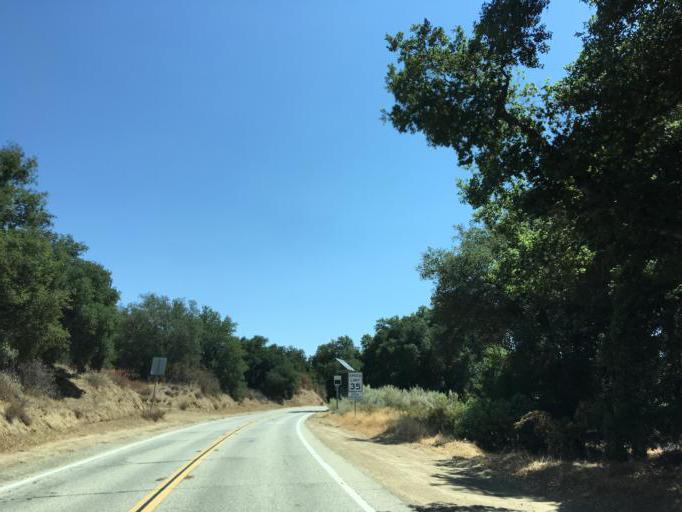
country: US
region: California
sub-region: Los Angeles County
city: Green Valley
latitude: 34.6166
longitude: -118.4226
